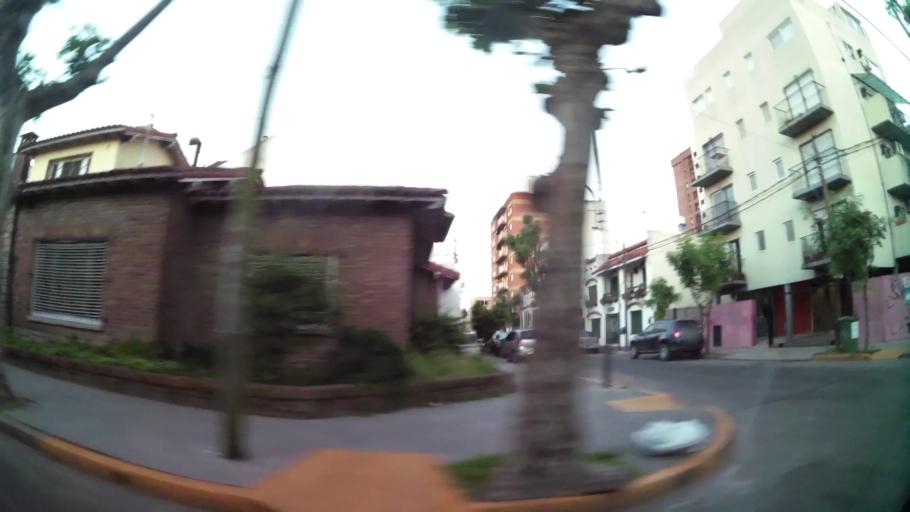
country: AR
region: Buenos Aires
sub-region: Partido de Tigre
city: Tigre
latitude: -34.4436
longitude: -58.5549
